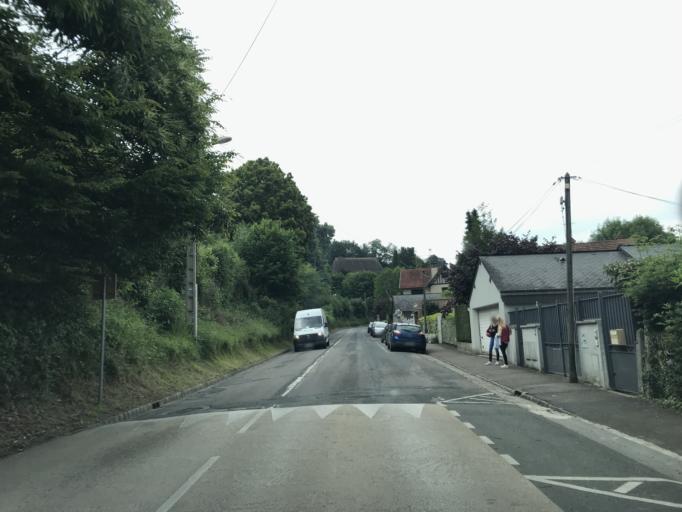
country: FR
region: Haute-Normandie
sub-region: Departement de la Seine-Maritime
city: Mont-Saint-Aignan
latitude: 49.4561
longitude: 1.0843
